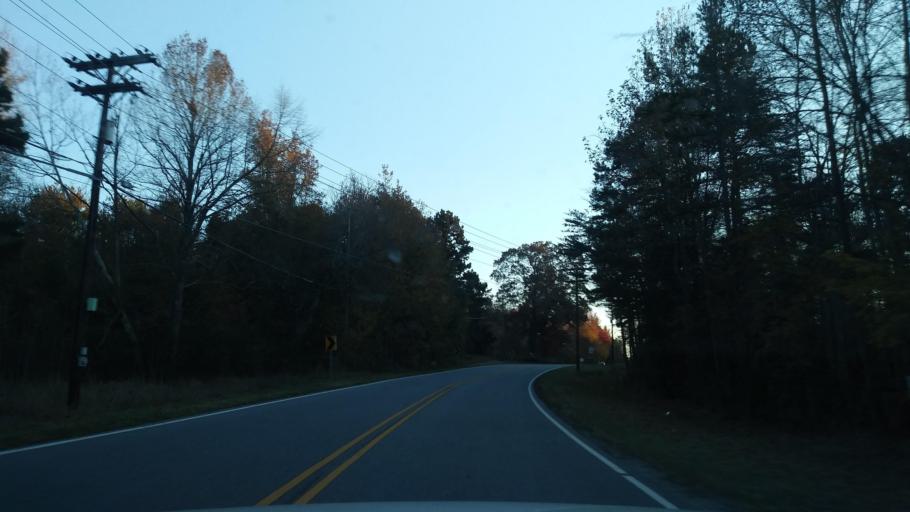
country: US
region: North Carolina
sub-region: Guilford County
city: Pleasant Garden
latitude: 35.9971
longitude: -79.7770
